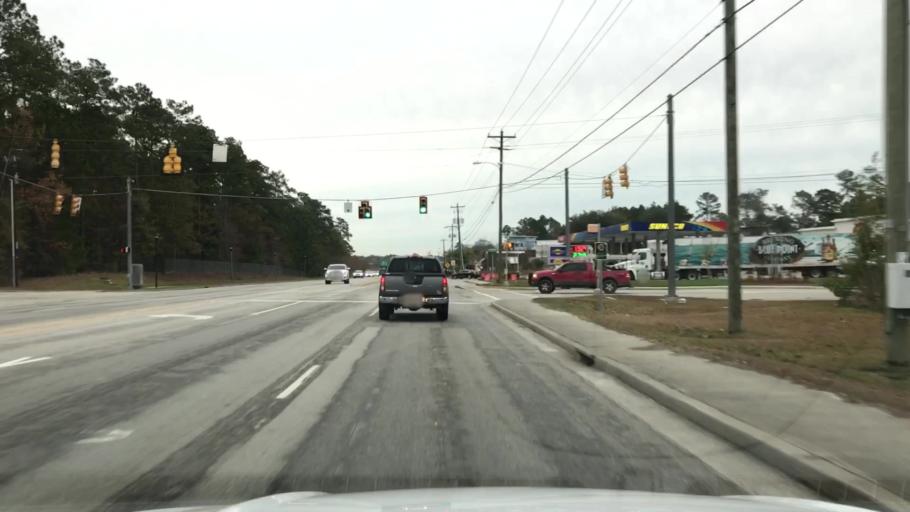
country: US
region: South Carolina
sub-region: Berkeley County
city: Goose Creek
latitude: 32.9745
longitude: -80.0599
